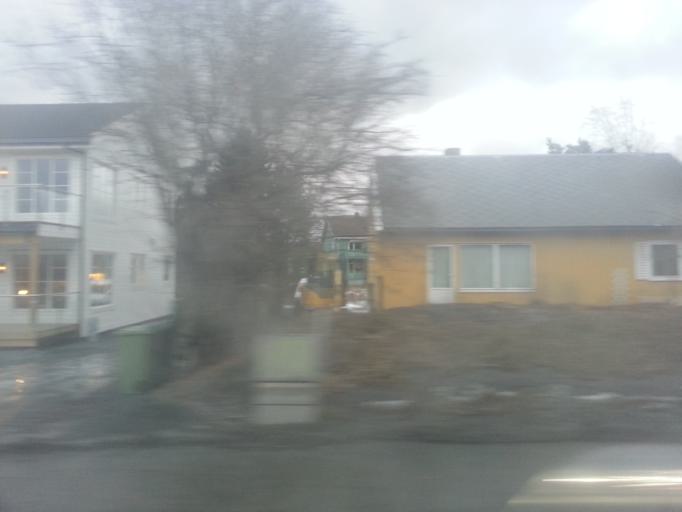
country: NO
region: Sor-Trondelag
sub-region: Trondheim
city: Trondheim
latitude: 63.4311
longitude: 10.4550
